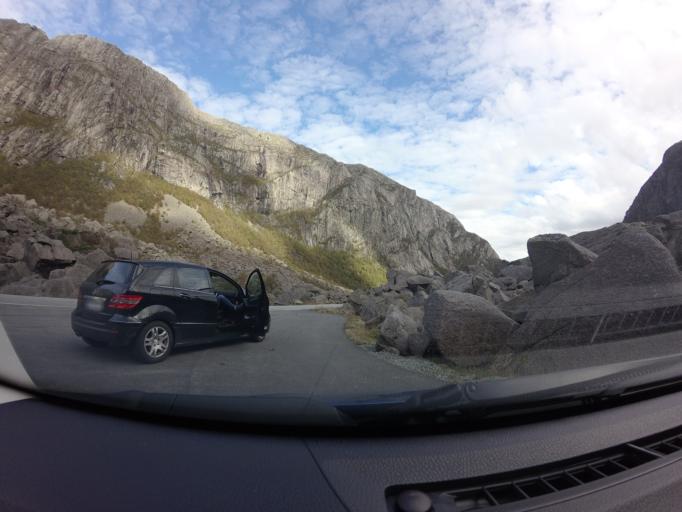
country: NO
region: Rogaland
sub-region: Forsand
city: Forsand
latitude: 58.7676
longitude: 6.2797
